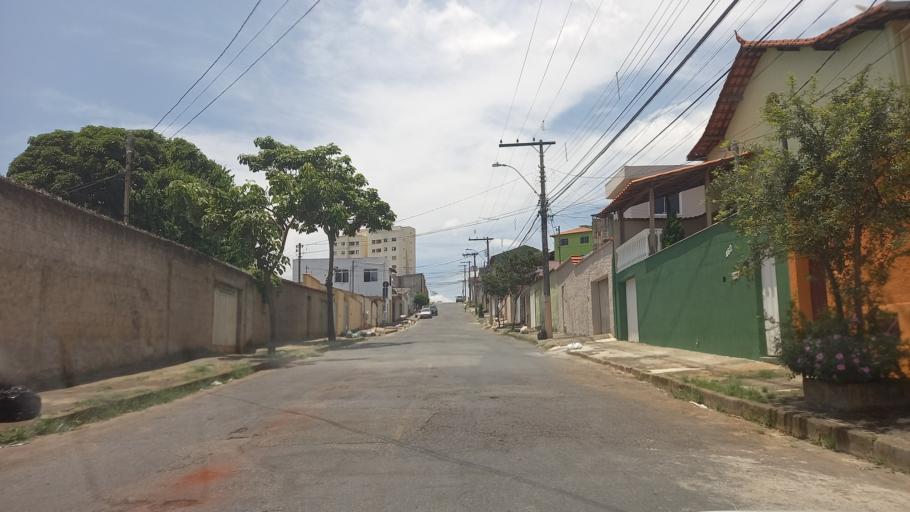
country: BR
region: Minas Gerais
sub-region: Contagem
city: Contagem
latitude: -19.9116
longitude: -44.0045
